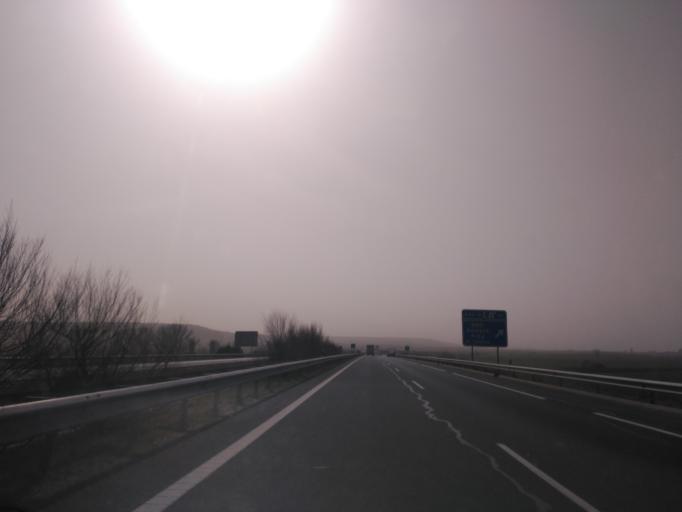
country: ES
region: Castille and Leon
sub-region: Provincia de Palencia
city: Pina de Campos
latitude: 42.1996
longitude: -4.4490
